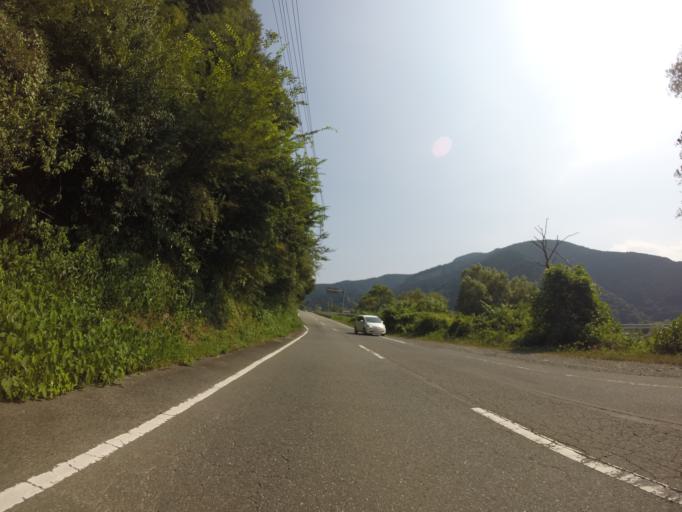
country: JP
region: Shizuoka
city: Shizuoka-shi
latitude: 35.1152
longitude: 138.3609
